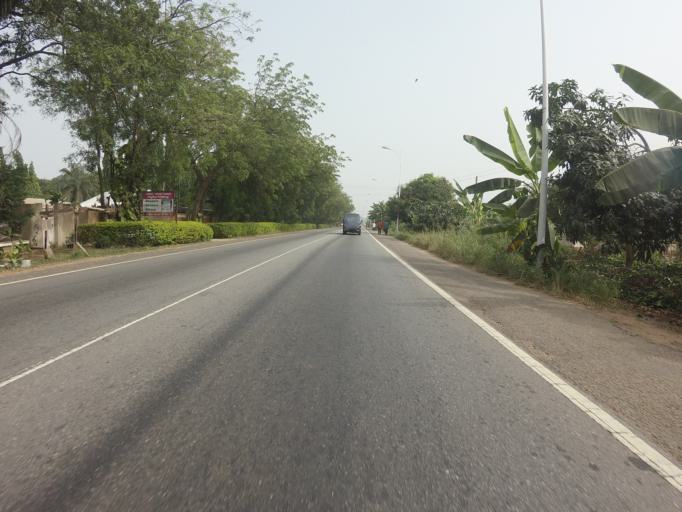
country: GH
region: Volta
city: Anloga
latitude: 6.0072
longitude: 0.5558
